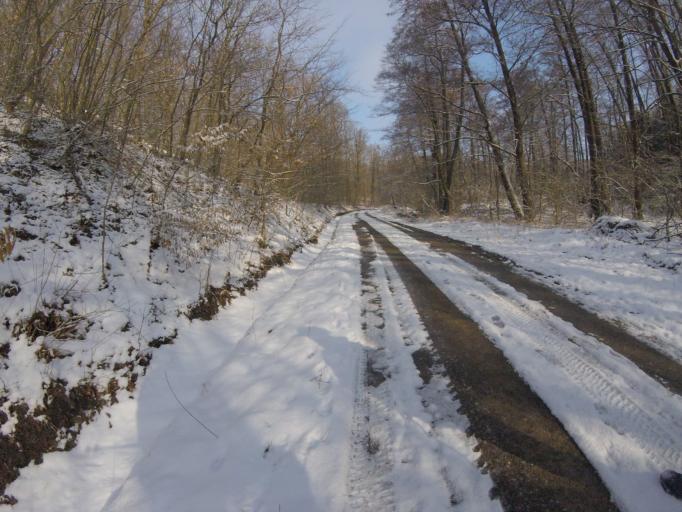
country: HU
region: Heves
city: Belapatfalva
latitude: 48.0601
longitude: 20.3759
